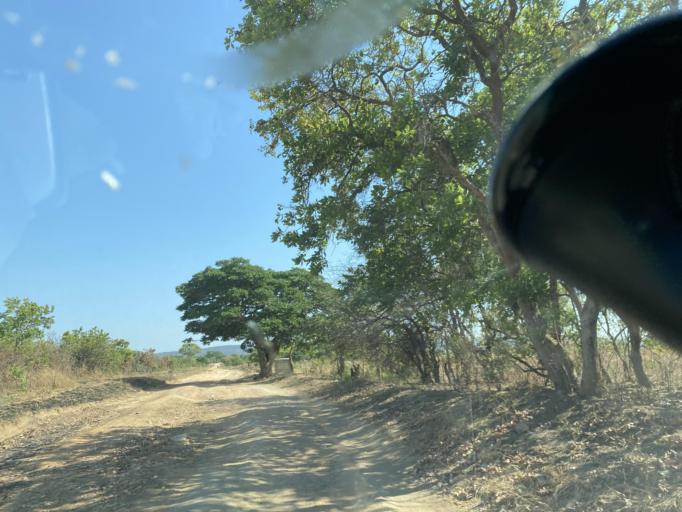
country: ZM
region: Lusaka
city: Chongwe
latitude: -15.2318
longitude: 28.8400
